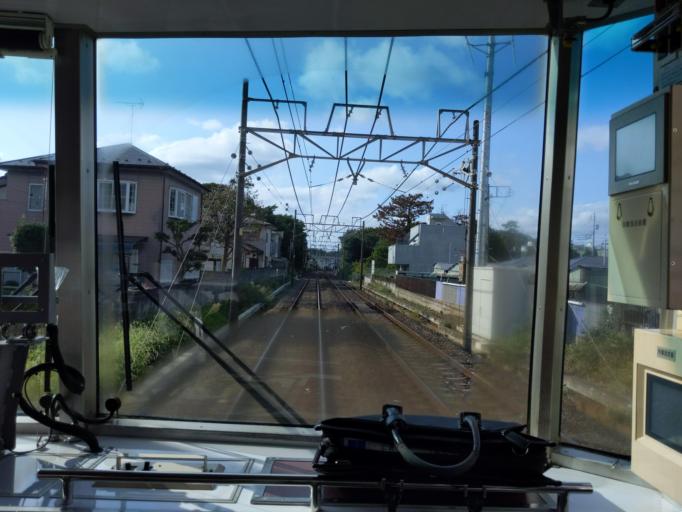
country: JP
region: Chiba
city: Shiroi
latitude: 35.7587
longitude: 140.0117
